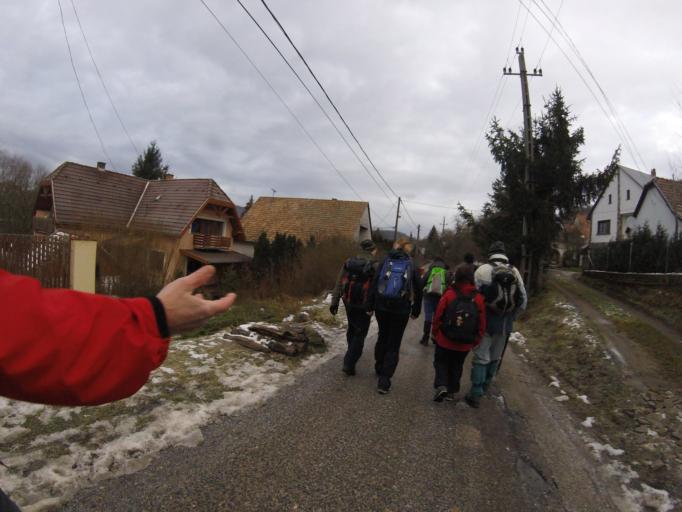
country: HU
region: Pest
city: Visegrad
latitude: 47.7250
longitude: 18.9903
